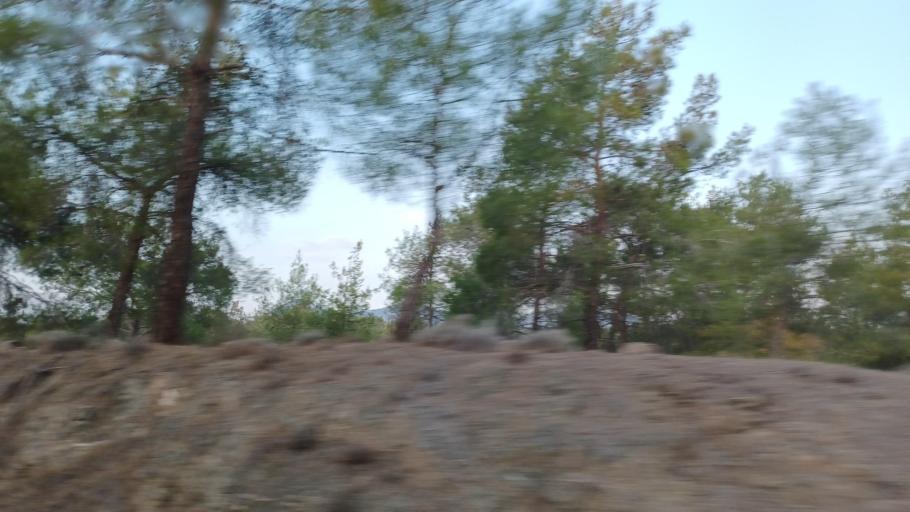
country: CY
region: Larnaka
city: Kornos
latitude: 34.9114
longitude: 33.3581
